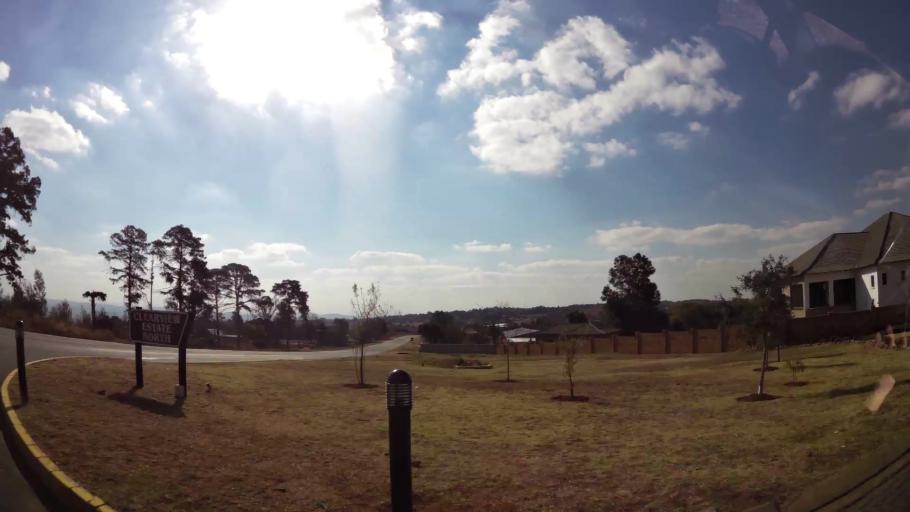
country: ZA
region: Gauteng
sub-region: West Rand District Municipality
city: Krugersdorp
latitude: -26.0544
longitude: 27.7544
